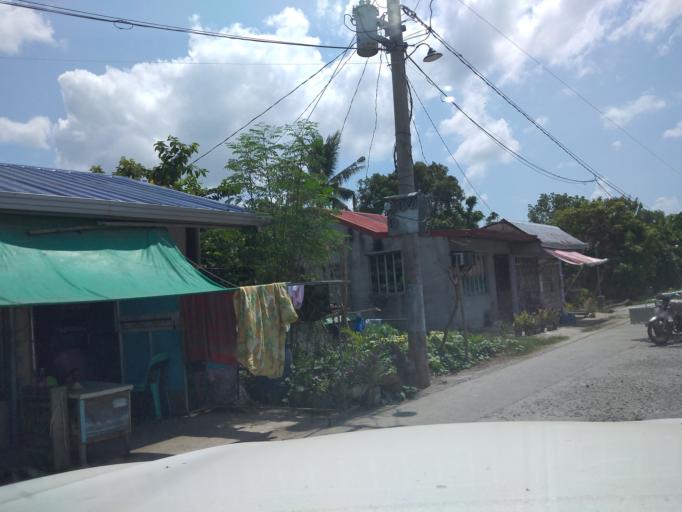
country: PH
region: Central Luzon
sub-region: Province of Pampanga
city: Lourdes
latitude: 15.0158
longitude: 120.8657
